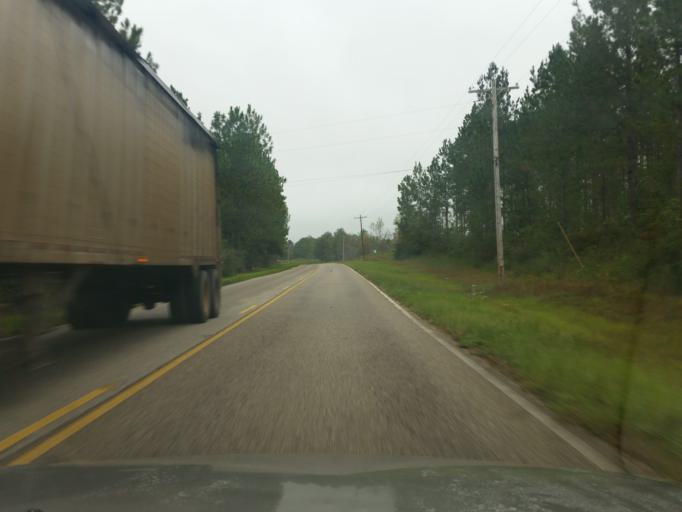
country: US
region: Florida
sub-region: Escambia County
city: Cantonment
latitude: 30.6520
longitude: -87.4501
